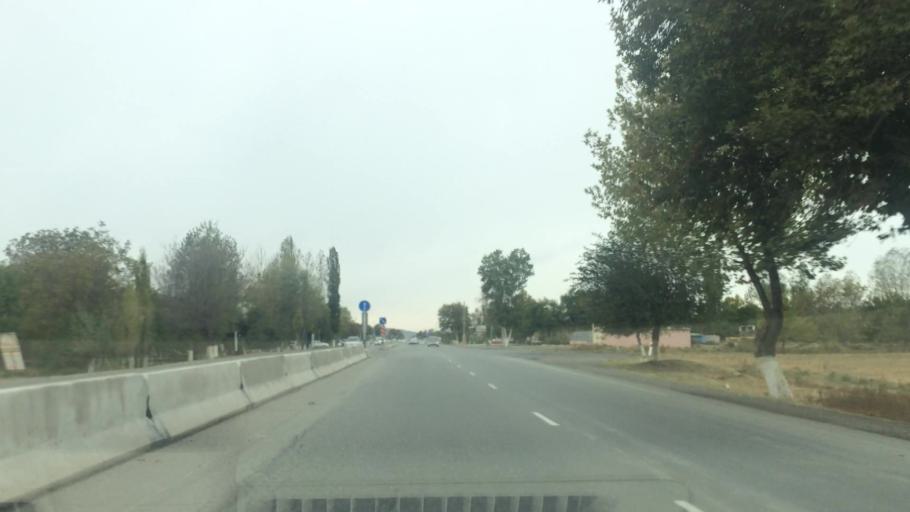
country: UZ
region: Samarqand
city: Jomboy
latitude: 39.7171
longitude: 67.1100
